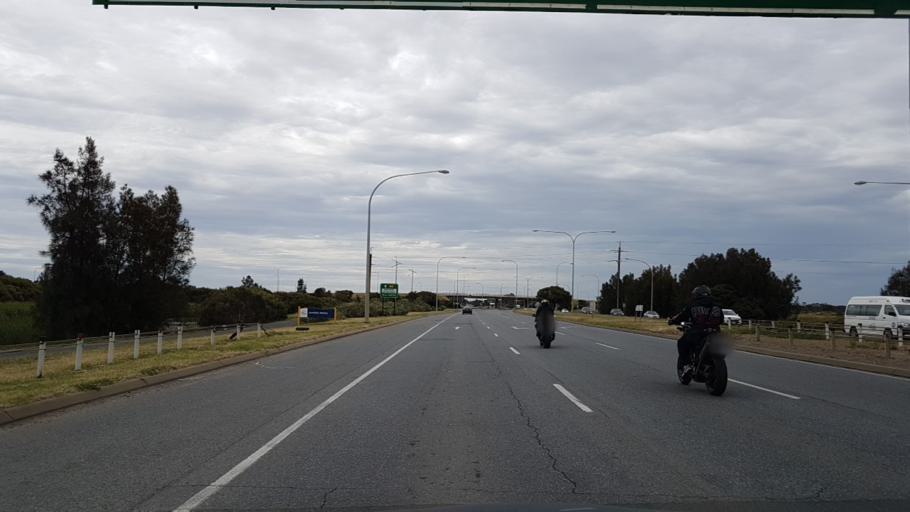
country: AU
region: South Australia
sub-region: Port Adelaide Enfield
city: Enfield
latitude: -34.8157
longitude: 138.5976
